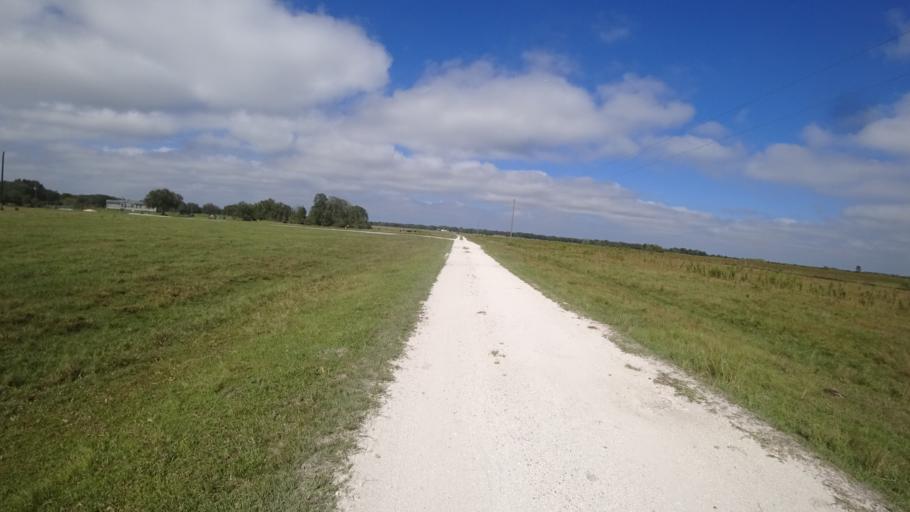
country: US
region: Florida
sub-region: DeSoto County
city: Arcadia
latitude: 27.3217
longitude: -82.1097
